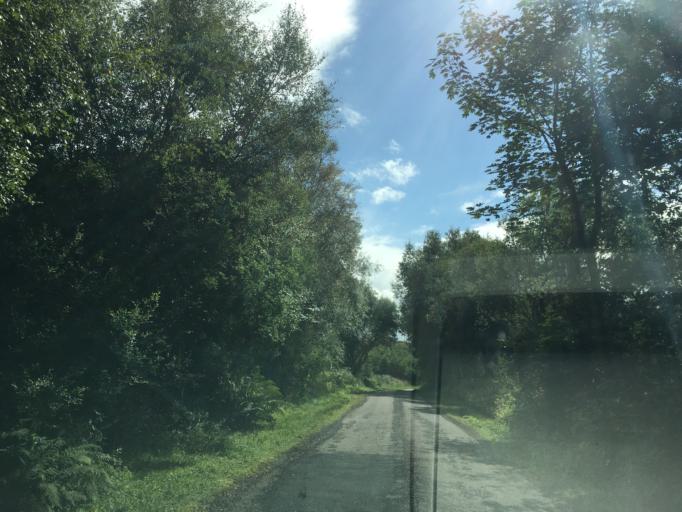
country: GB
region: Scotland
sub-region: Argyll and Bute
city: Oban
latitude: 56.4521
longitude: -5.4051
